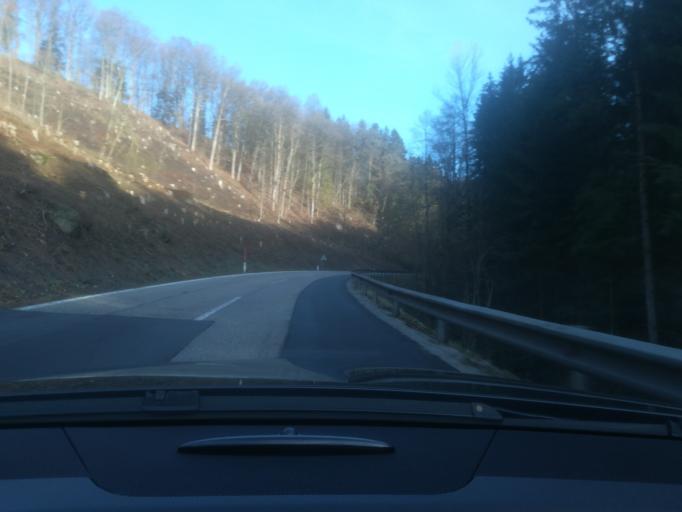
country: AT
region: Upper Austria
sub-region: Politischer Bezirk Urfahr-Umgebung
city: Feldkirchen an der Donau
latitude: 48.3832
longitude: 14.0786
